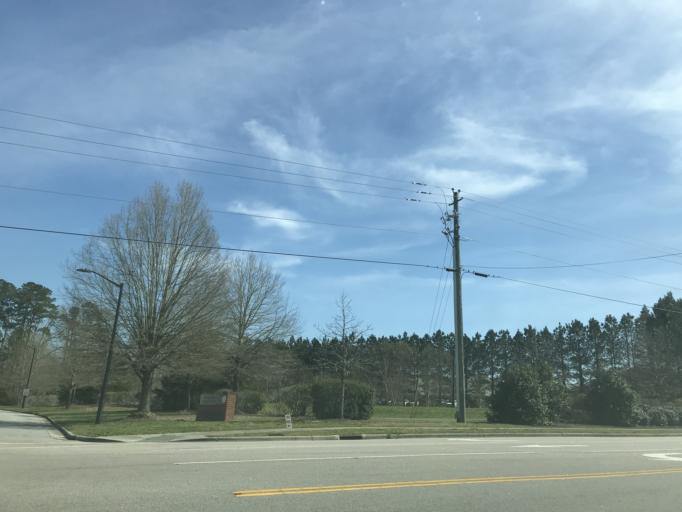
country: US
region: North Carolina
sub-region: Wake County
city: Knightdale
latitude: 35.8120
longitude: -78.4821
